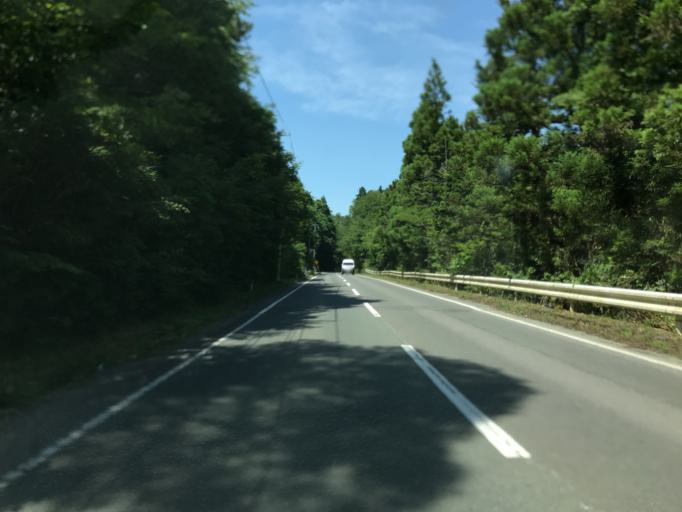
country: JP
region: Miyagi
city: Marumori
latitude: 37.7435
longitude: 140.9151
